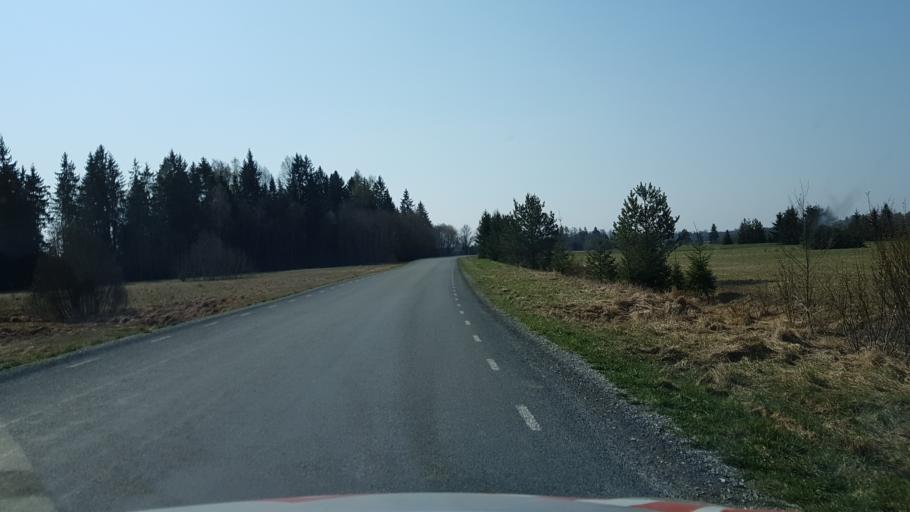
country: EE
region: Raplamaa
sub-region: Maerjamaa vald
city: Marjamaa
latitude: 58.8650
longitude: 24.3718
